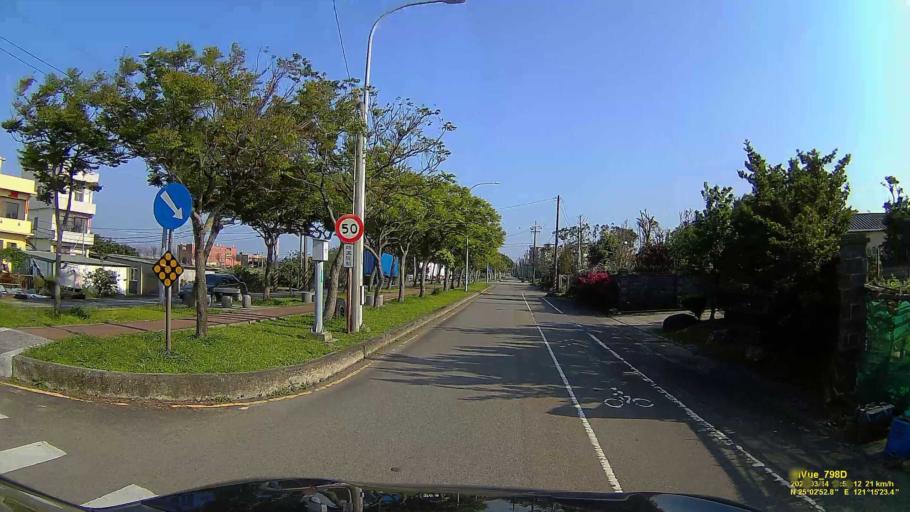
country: TW
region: Taiwan
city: Taoyuan City
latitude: 25.0479
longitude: 121.2565
